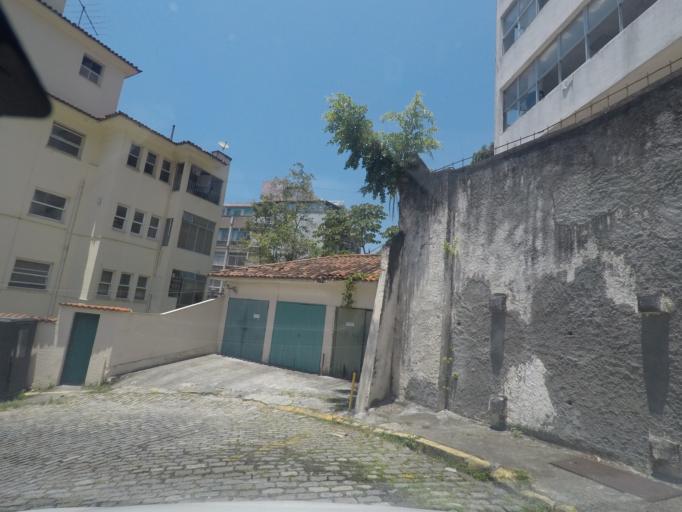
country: BR
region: Rio de Janeiro
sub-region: Rio De Janeiro
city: Rio de Janeiro
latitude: -22.9647
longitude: -43.1839
